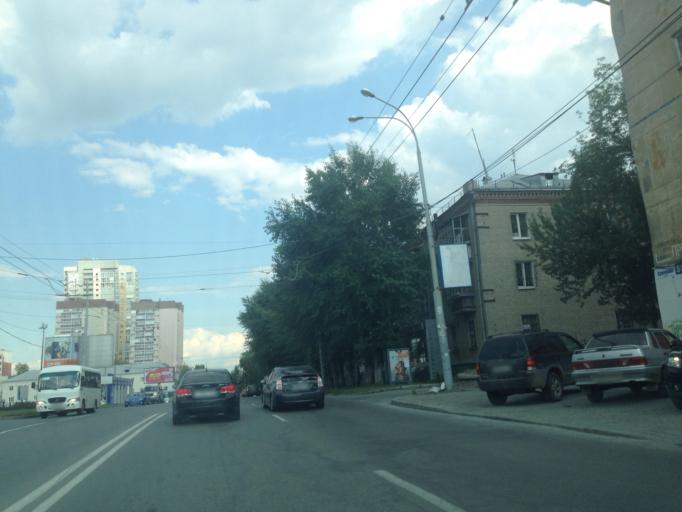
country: RU
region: Sverdlovsk
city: Yekaterinburg
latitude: 56.8625
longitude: 60.6296
